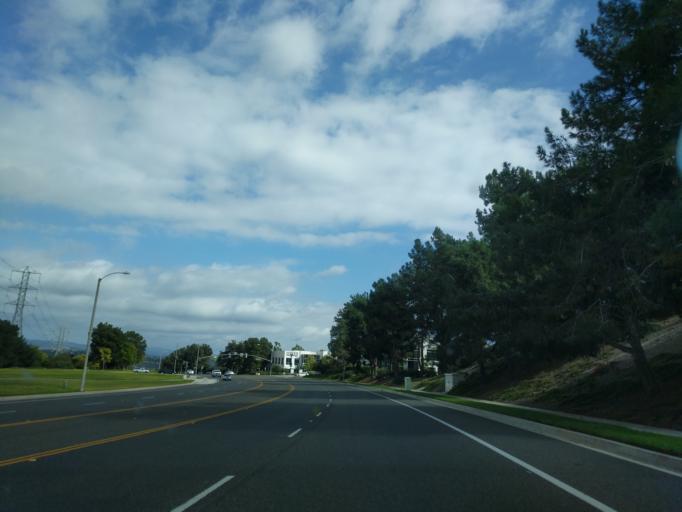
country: US
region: California
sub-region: Orange County
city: Laguna Woods
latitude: 33.5912
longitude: -117.7268
